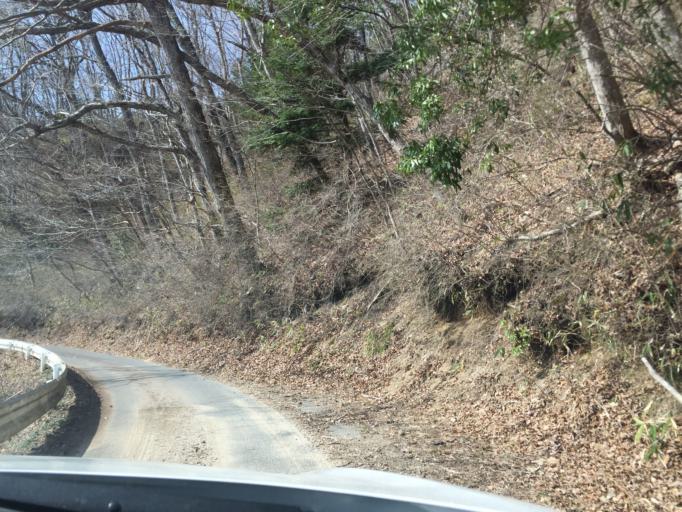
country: JP
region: Fukushima
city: Iwaki
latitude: 37.1289
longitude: 140.7830
